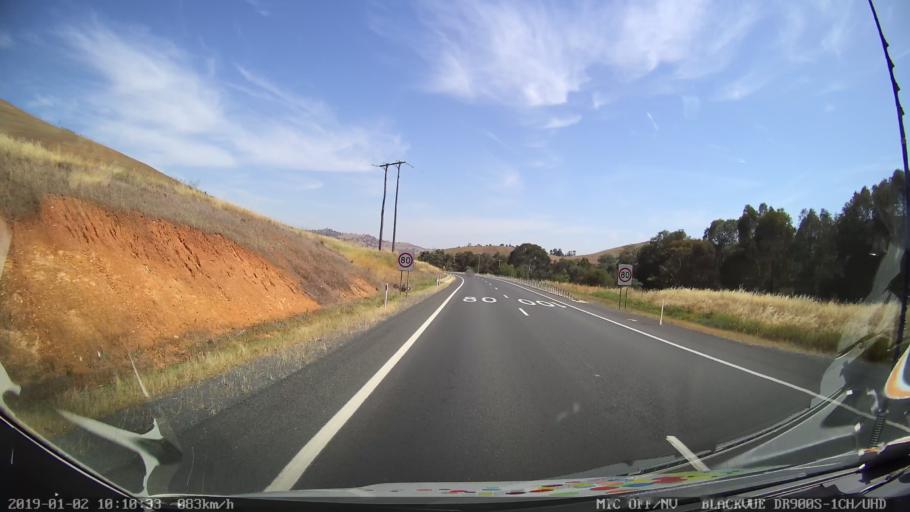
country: AU
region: New South Wales
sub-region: Gundagai
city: Gundagai
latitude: -35.1024
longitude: 148.0961
